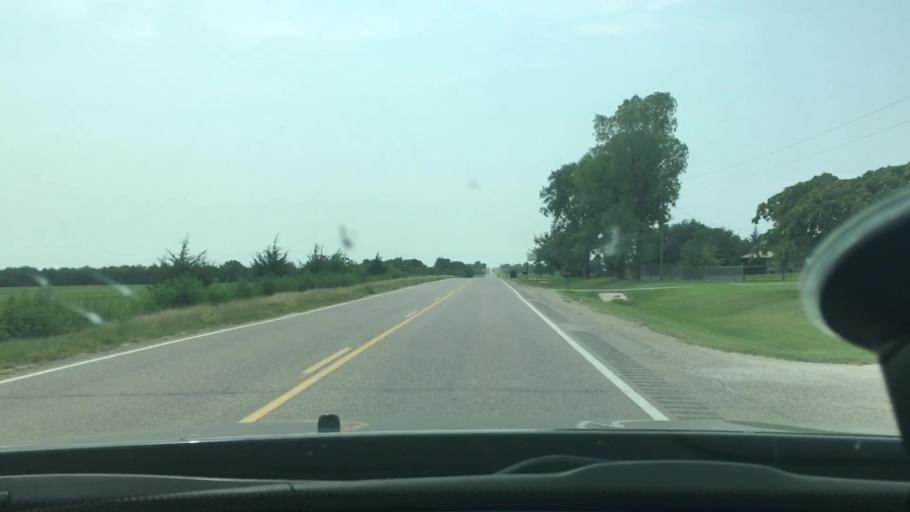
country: US
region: Oklahoma
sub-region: Marshall County
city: Madill
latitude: 34.0470
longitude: -96.7611
